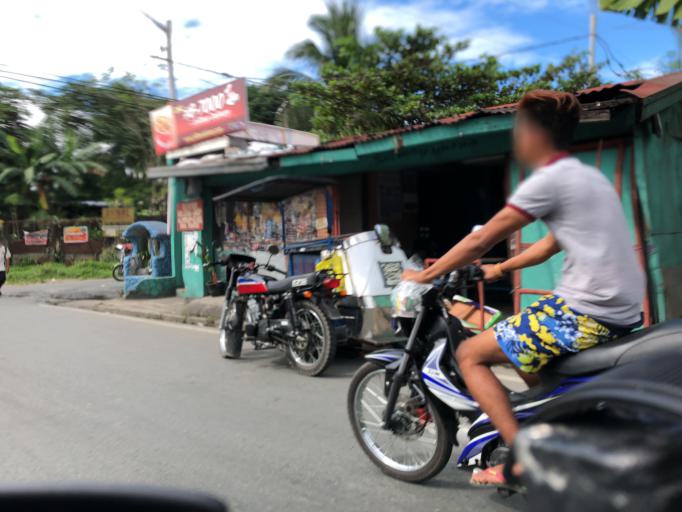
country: PH
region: Central Luzon
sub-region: Province of Bulacan
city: San Jose del Monte
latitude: 14.7585
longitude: 121.0530
